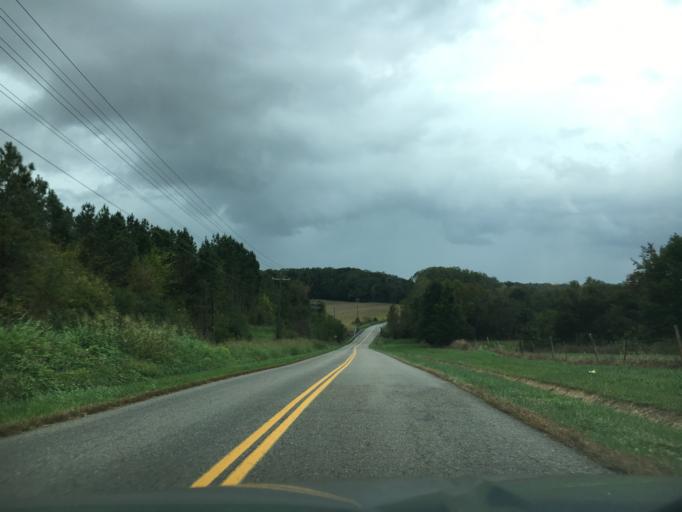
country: US
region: Virginia
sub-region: Amelia County
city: Amelia Court House
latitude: 37.3831
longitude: -77.9790
